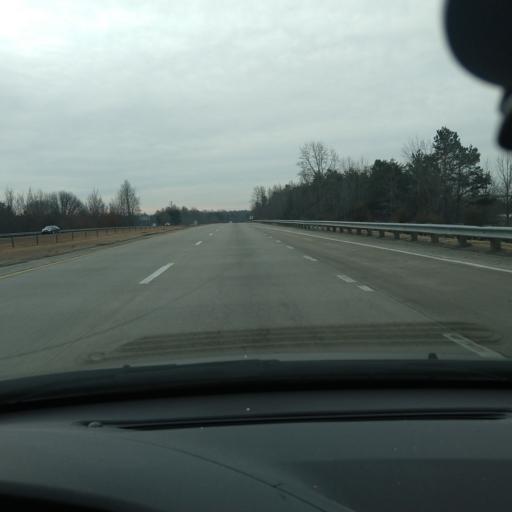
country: US
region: North Carolina
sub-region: Davidson County
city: Midway
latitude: 35.9361
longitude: -80.2334
